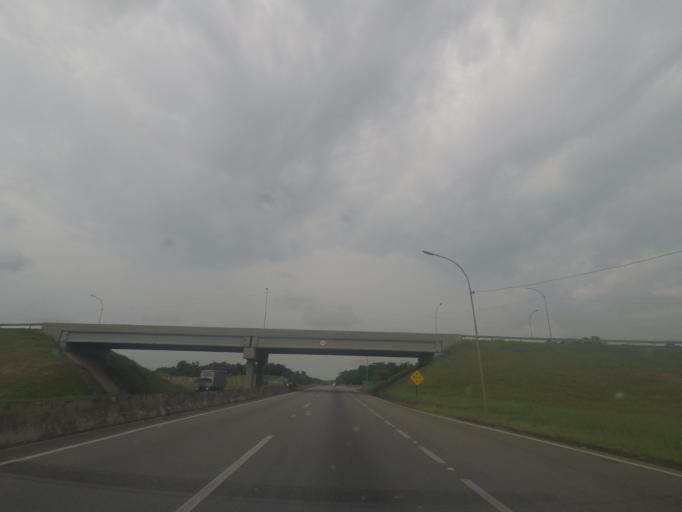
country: BR
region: Sao Paulo
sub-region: Registro
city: Registro
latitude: -24.5385
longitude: -47.8597
